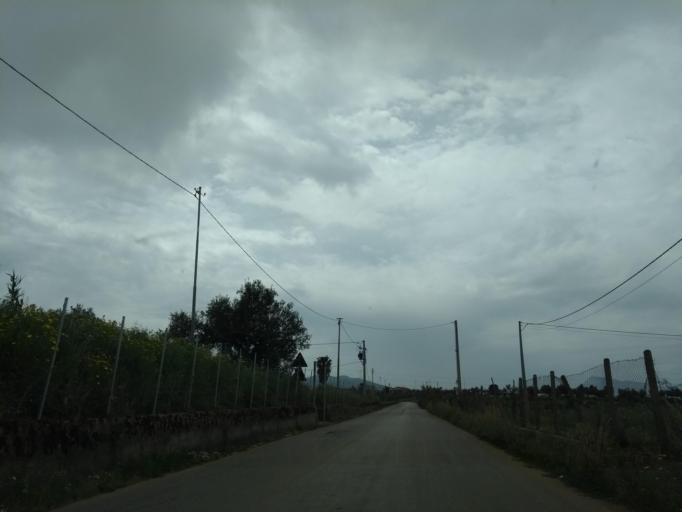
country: IT
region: Sicily
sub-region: Palermo
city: Partinico
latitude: 38.0010
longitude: 13.0673
